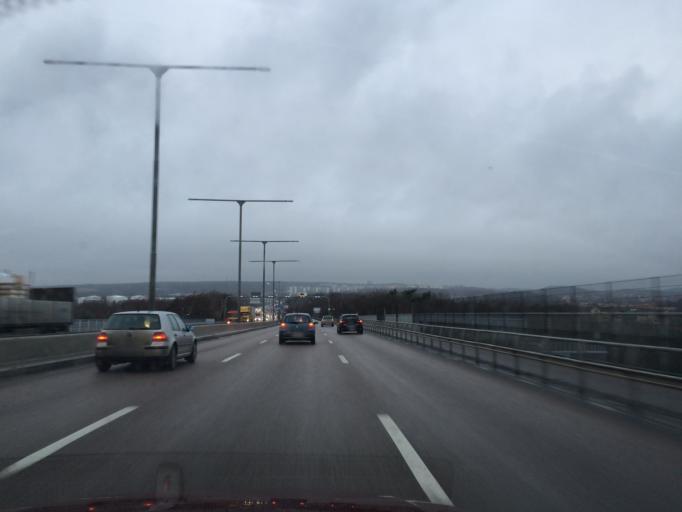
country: SE
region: Vaestra Goetaland
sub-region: Goteborg
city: Majorna
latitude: 57.6935
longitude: 11.9001
